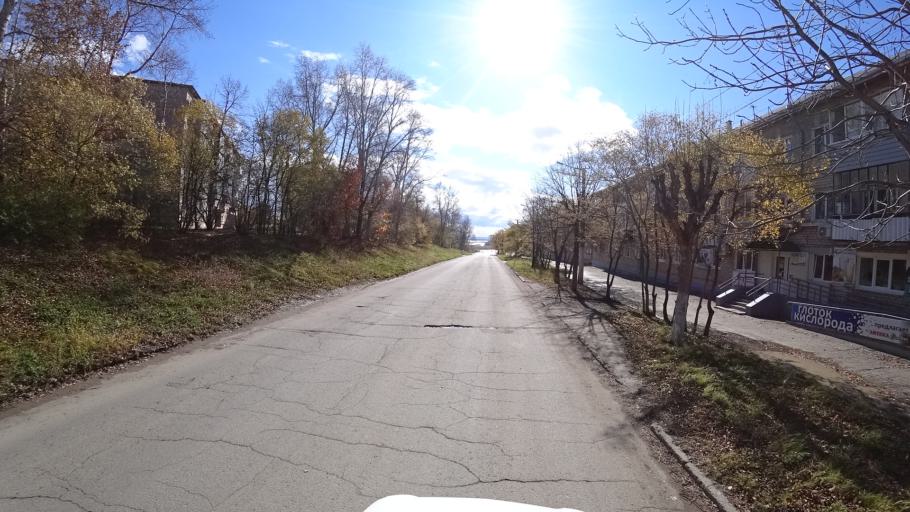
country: RU
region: Khabarovsk Krai
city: Amursk
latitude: 50.2173
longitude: 136.9032
